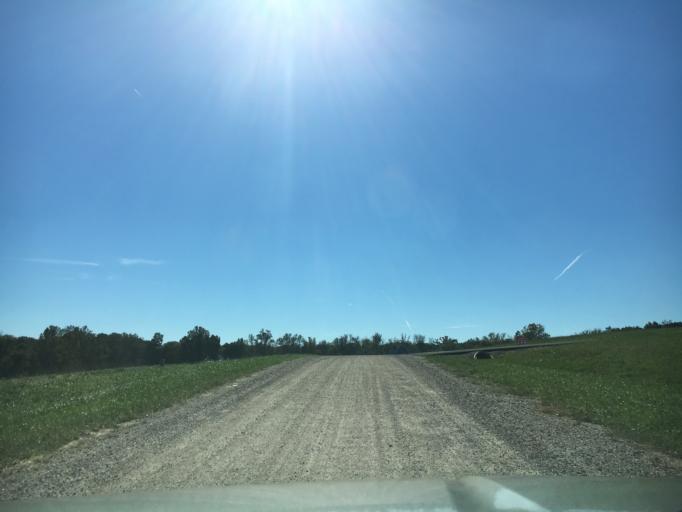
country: US
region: Virginia
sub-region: Goochland County
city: Goochland
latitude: 37.6924
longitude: -77.8306
